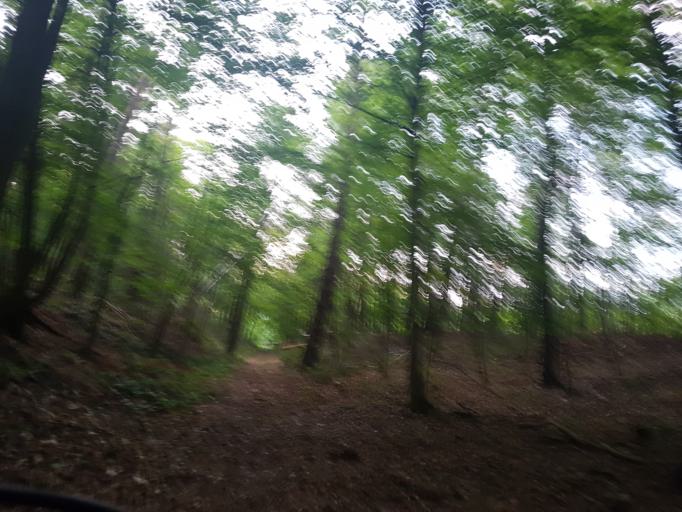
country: DE
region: Brandenburg
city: Trobitz
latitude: 51.5802
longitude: 13.4180
